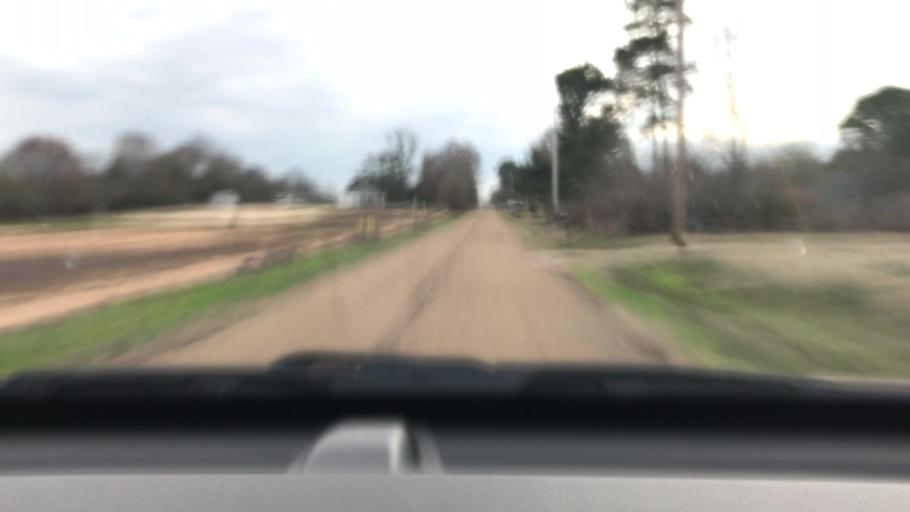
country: US
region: Arkansas
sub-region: Hempstead County
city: Hope
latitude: 33.6386
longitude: -93.5617
